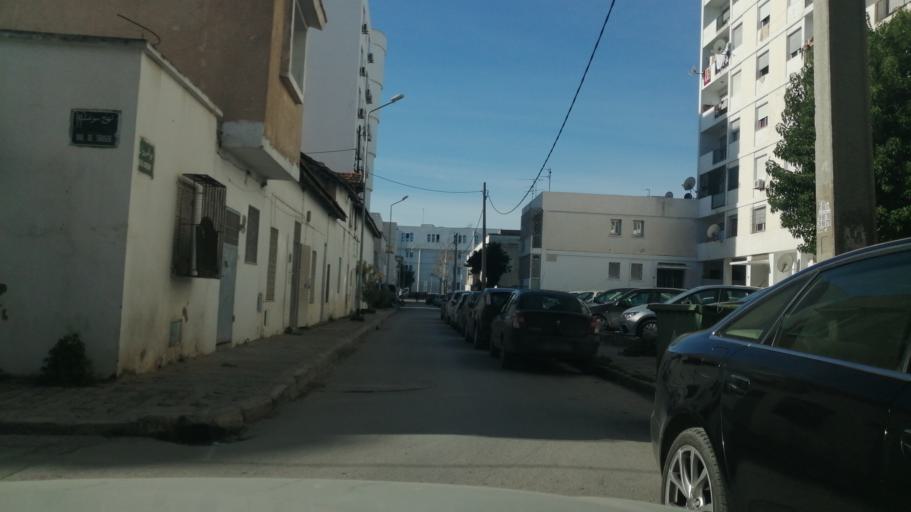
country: TN
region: Tunis
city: Tunis
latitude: 36.8132
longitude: 10.1713
